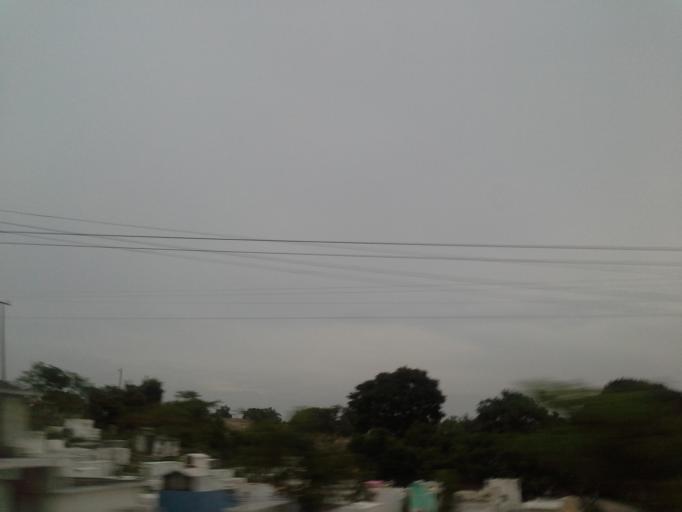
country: CO
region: Sucre
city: Morroa
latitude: 9.3527
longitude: -75.2855
